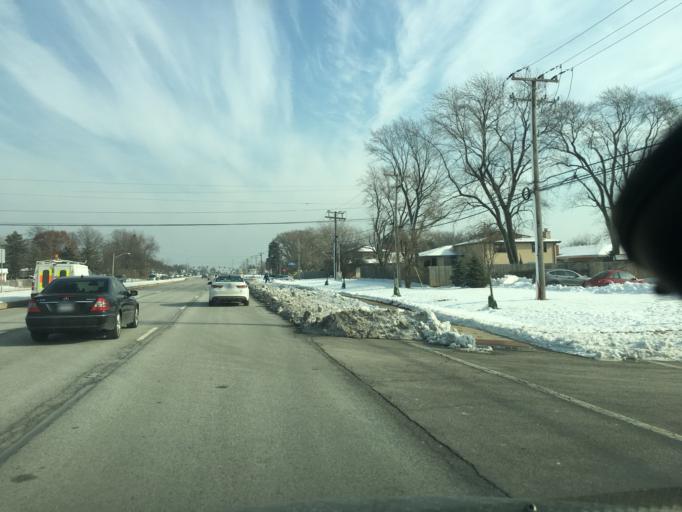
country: US
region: Illinois
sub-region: DuPage County
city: Darien
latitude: 41.7511
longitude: -88.0086
